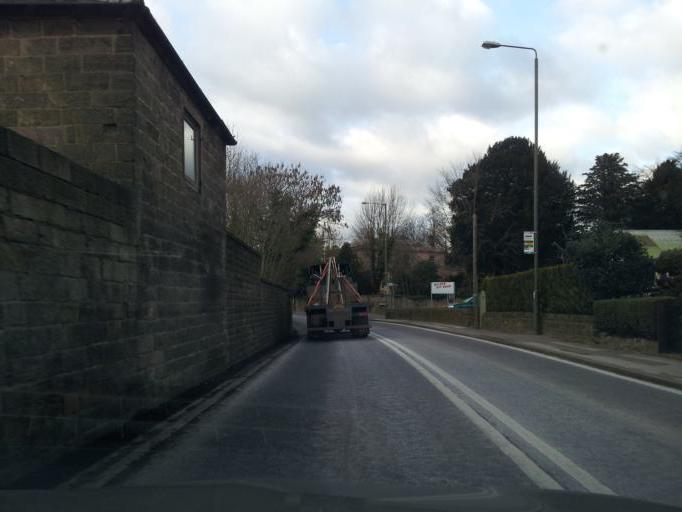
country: GB
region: England
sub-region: Derbyshire
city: Matlock
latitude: 53.1519
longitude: -1.5769
